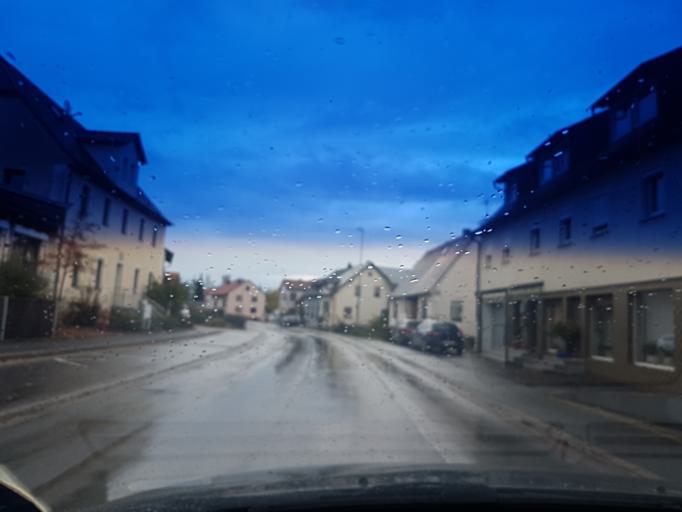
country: DE
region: Bavaria
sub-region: Regierungsbezirk Mittelfranken
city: Muhlhausen
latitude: 49.7552
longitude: 10.7776
